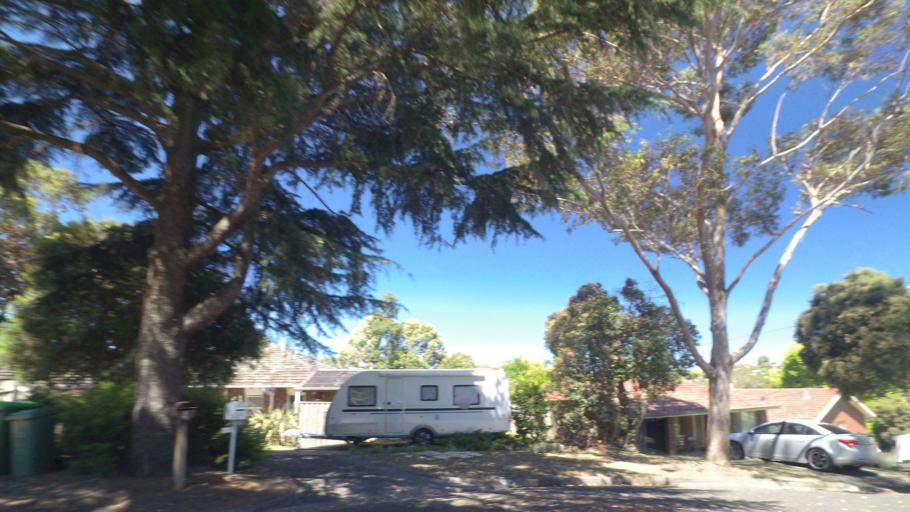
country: AU
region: Victoria
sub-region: Yarra Ranges
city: Chirnside Park
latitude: -37.7502
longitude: 145.3275
